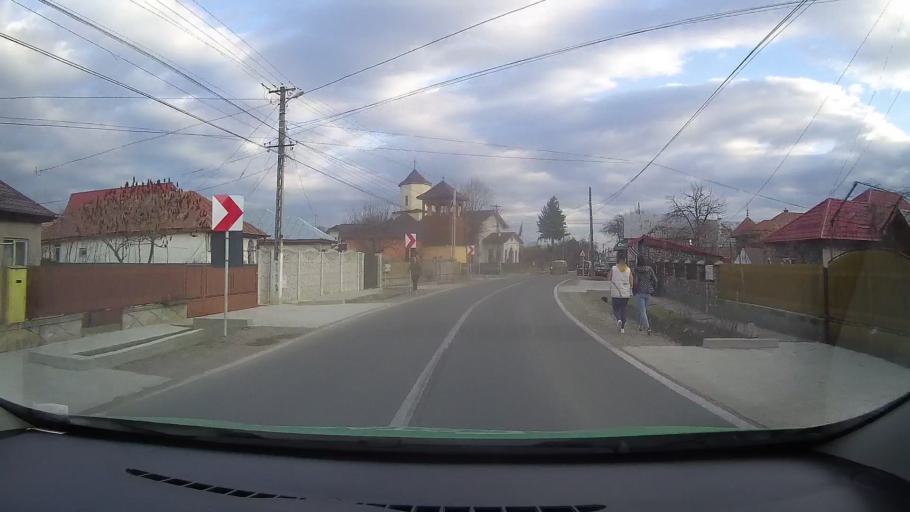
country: RO
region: Dambovita
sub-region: Comuna I. L. Caragiale
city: Ghirdoveni
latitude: 44.9343
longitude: 25.6848
